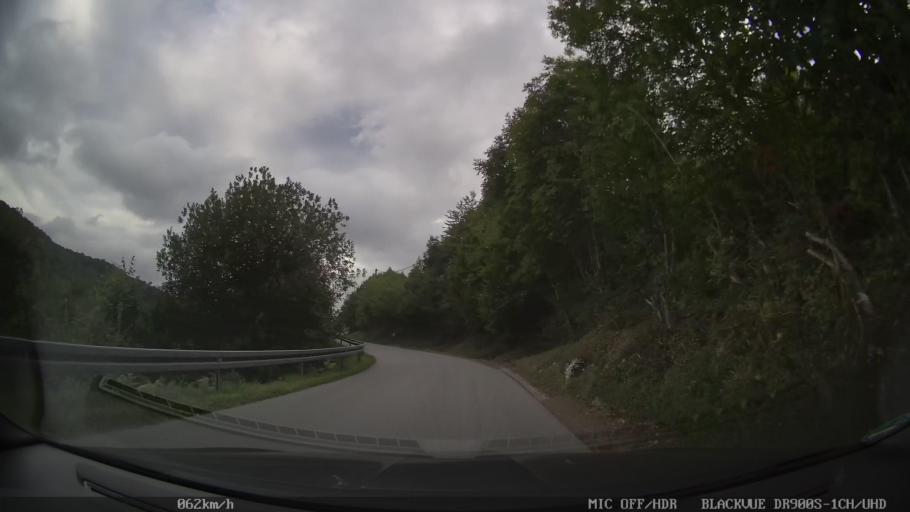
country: HR
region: Licko-Senjska
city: Jezerce
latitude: 44.9332
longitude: 15.6247
